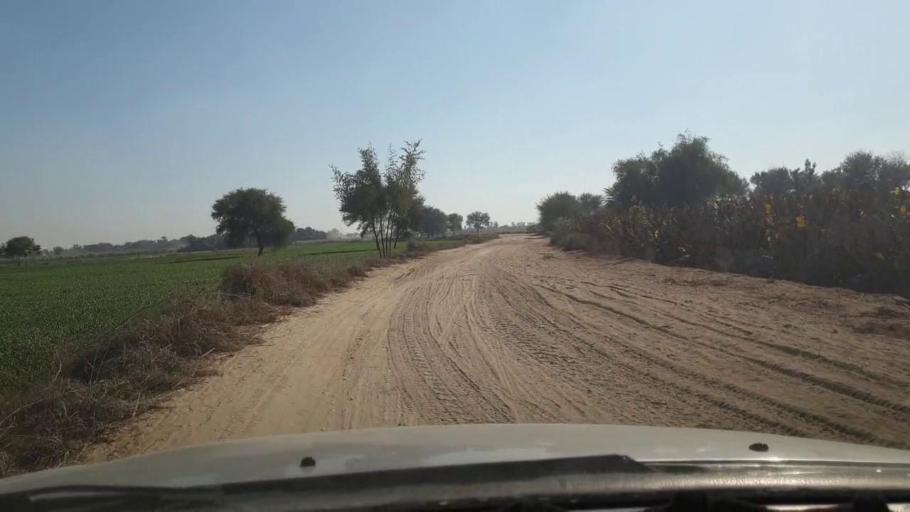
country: PK
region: Sindh
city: Ghotki
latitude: 28.0217
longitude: 69.2223
